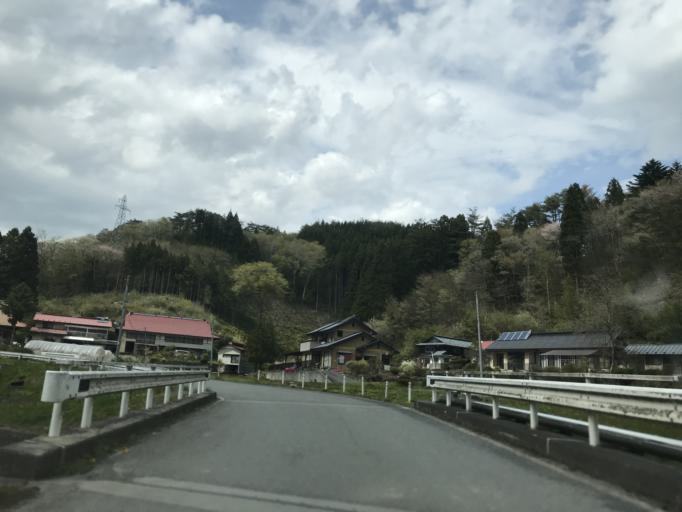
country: JP
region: Iwate
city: Ichinoseki
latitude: 38.7890
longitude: 141.4253
